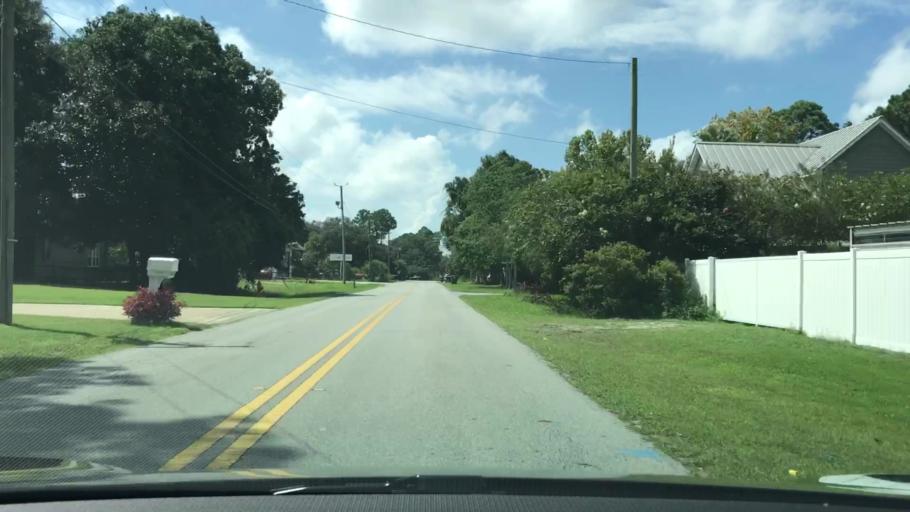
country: US
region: Florida
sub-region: Bay County
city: Panama City Beach
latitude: 30.1727
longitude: -85.7865
